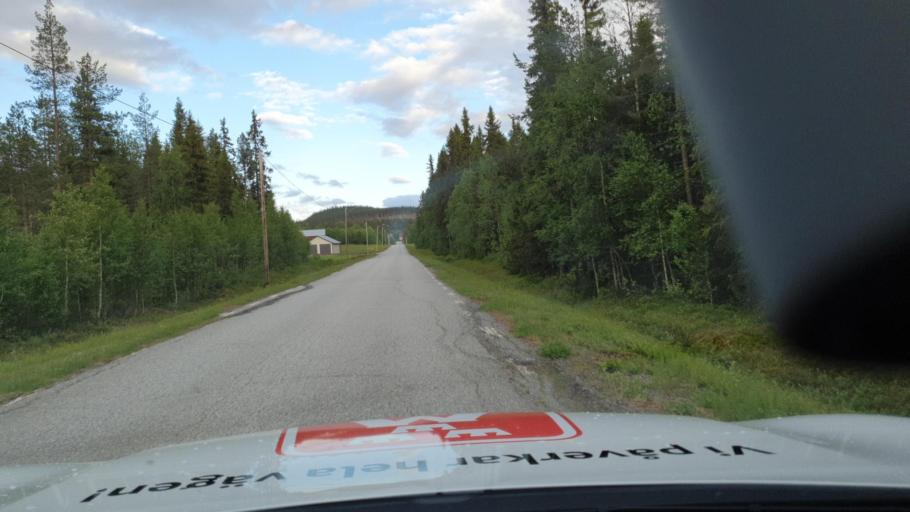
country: SE
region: Vaesterbotten
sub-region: Storumans Kommun
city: Storuman
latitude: 64.7071
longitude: 17.1084
